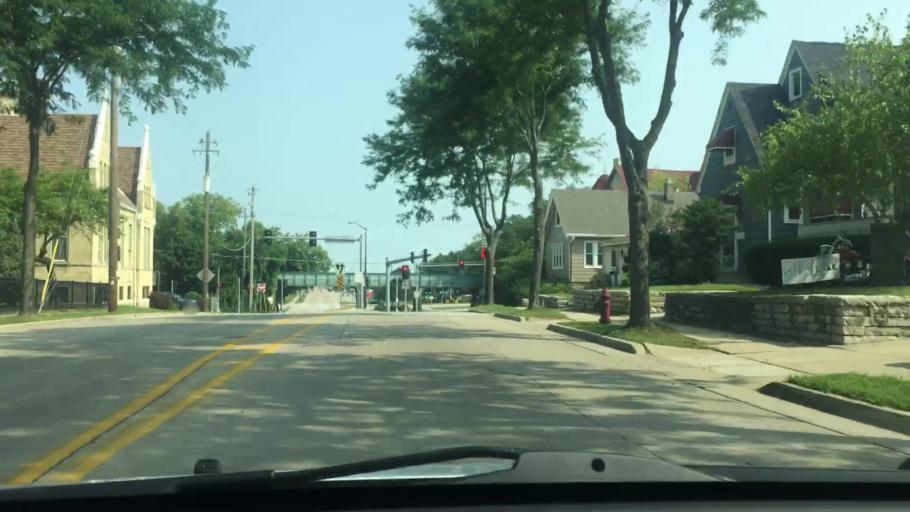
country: US
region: Wisconsin
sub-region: Milwaukee County
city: West Allis
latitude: 43.0088
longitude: -88.0171
